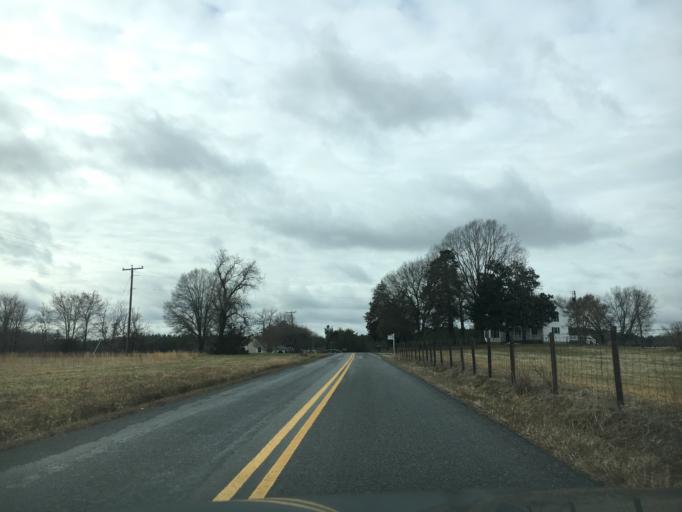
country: US
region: Virginia
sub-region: Halifax County
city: Mountain Road
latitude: 36.6804
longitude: -79.0282
